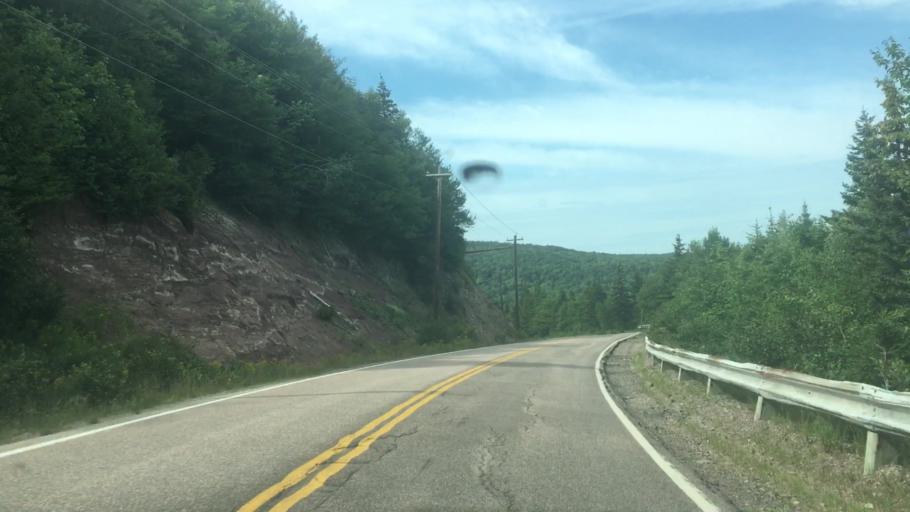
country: CA
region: Nova Scotia
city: Sydney Mines
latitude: 46.6029
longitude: -60.3854
